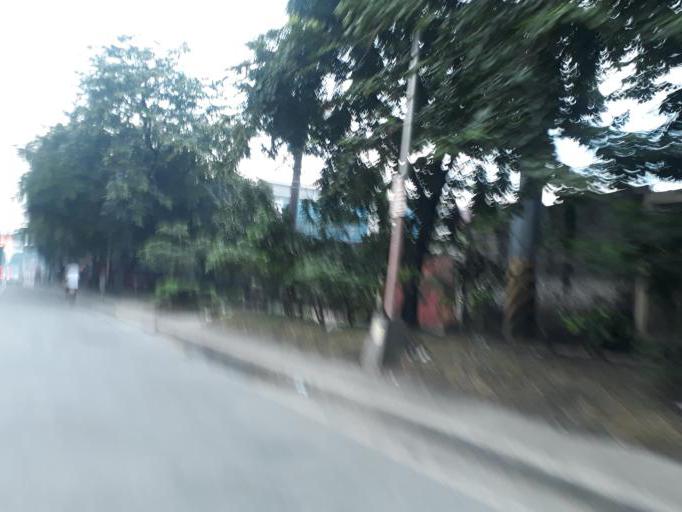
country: PH
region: Metro Manila
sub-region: Caloocan City
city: Niugan
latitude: 14.6583
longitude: 120.9628
